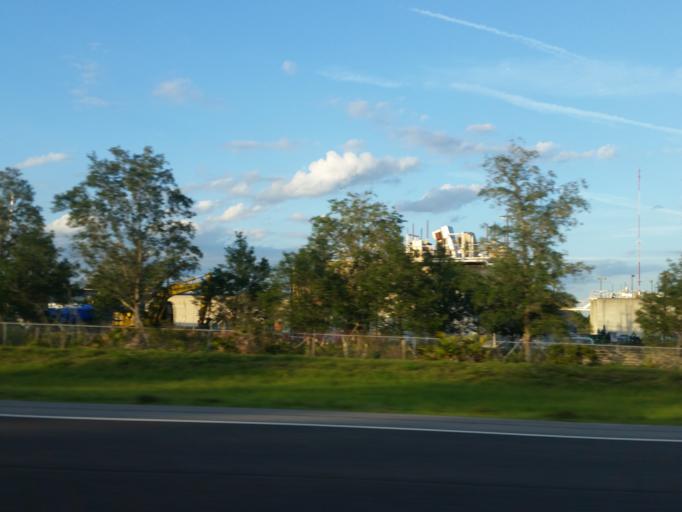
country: US
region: Florida
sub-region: Sarasota County
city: Nokomis
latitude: 27.1315
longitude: -82.4025
